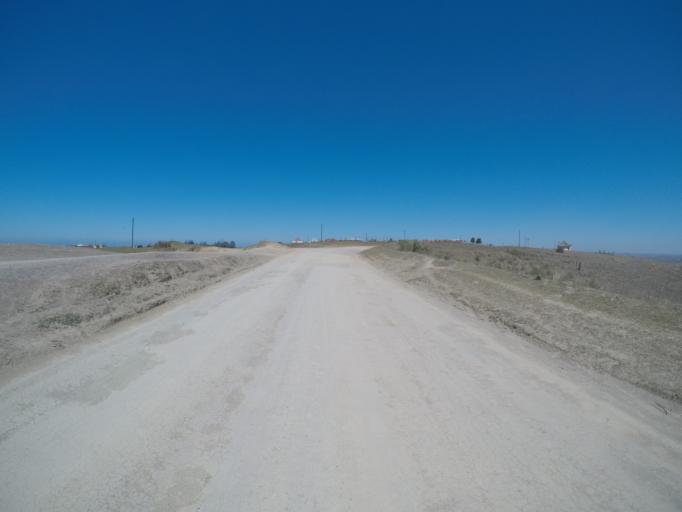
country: ZA
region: Eastern Cape
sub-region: OR Tambo District Municipality
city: Libode
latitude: -31.9438
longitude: 29.0274
